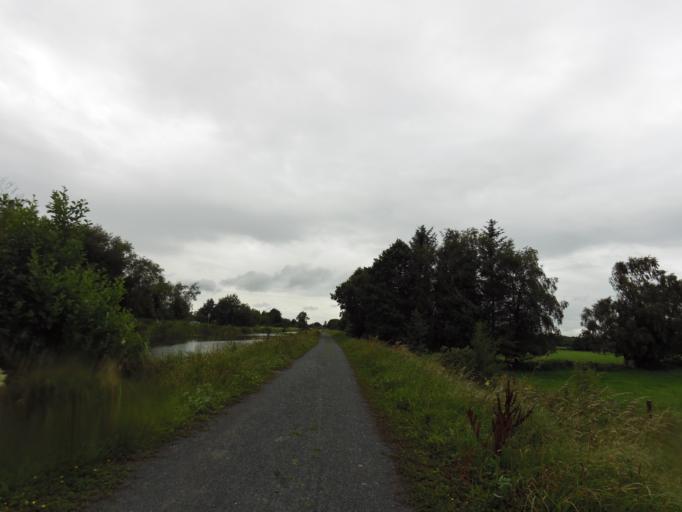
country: IE
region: Leinster
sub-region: An Iarmhi
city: Moate
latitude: 53.5882
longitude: -7.6353
